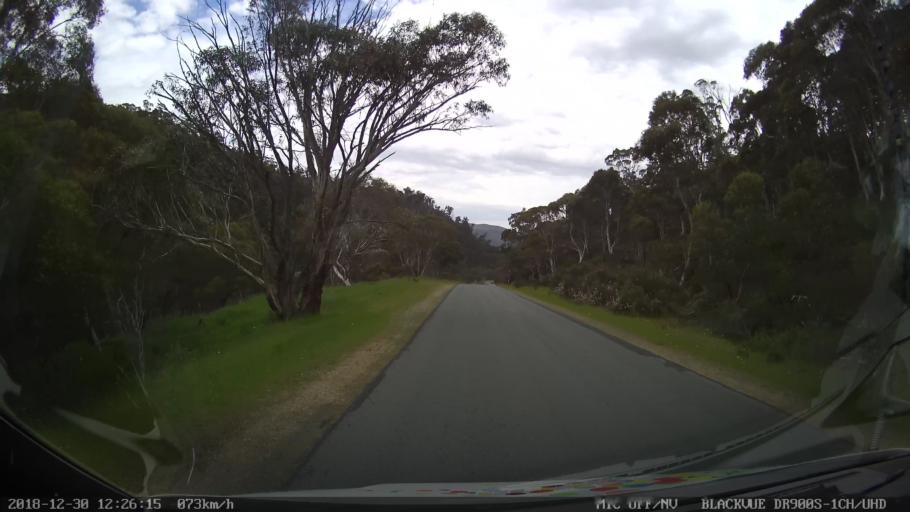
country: AU
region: New South Wales
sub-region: Snowy River
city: Jindabyne
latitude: -36.3413
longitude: 148.4892
